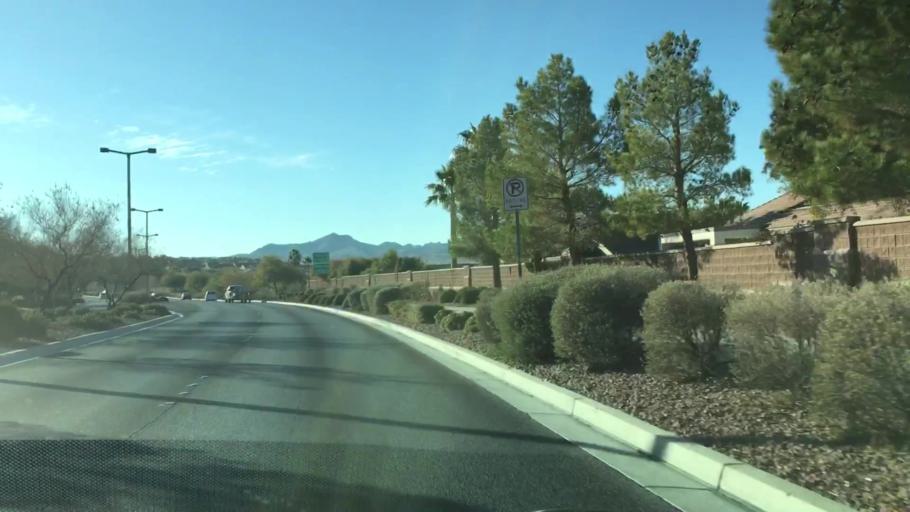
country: US
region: Nevada
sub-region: Clark County
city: Whitney
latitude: 35.9648
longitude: -115.1212
